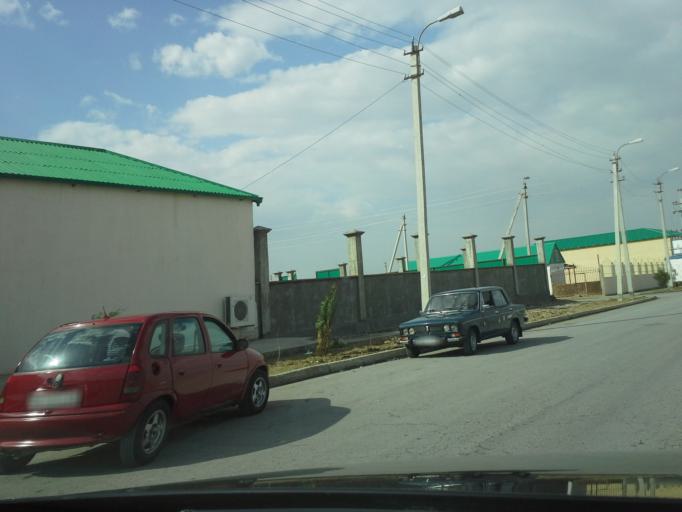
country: TM
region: Ahal
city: Abadan
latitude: 37.9738
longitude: 58.2720
